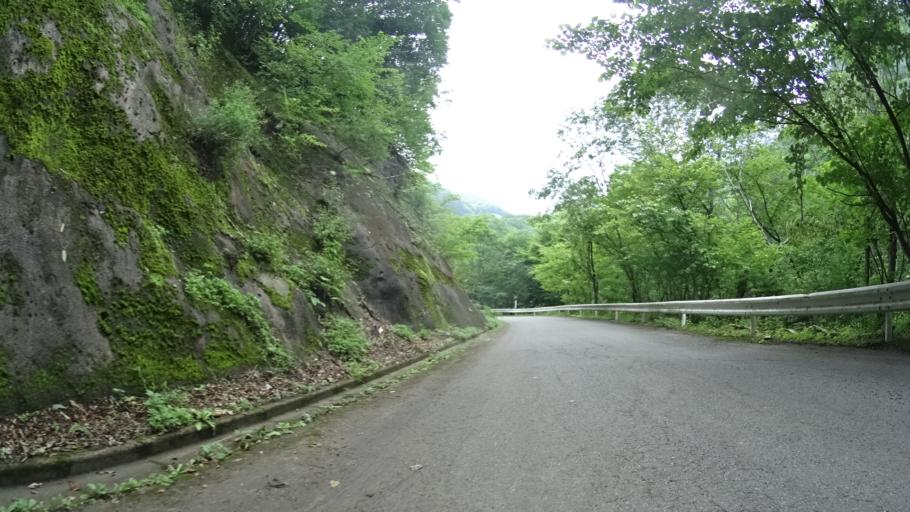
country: JP
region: Nagano
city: Saku
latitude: 36.0908
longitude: 138.6901
